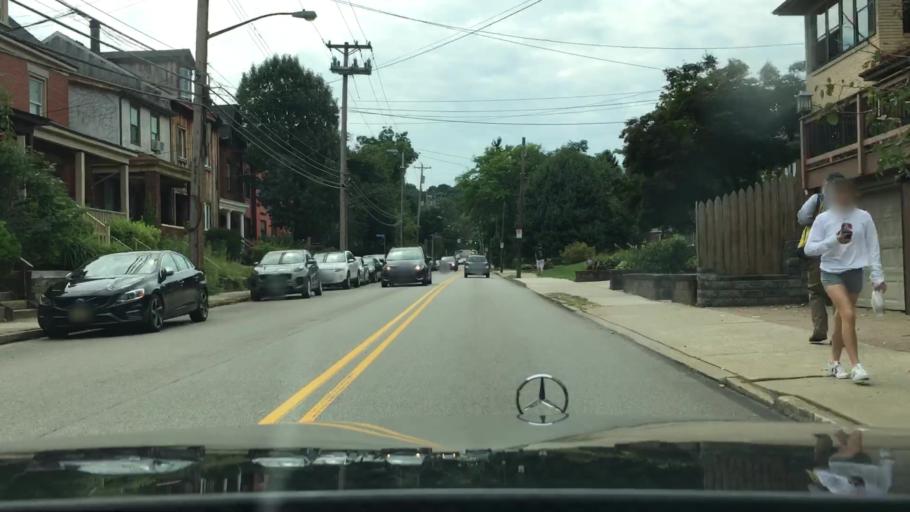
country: US
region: Pennsylvania
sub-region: Allegheny County
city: Bloomfield
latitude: 40.4524
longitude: -79.9366
